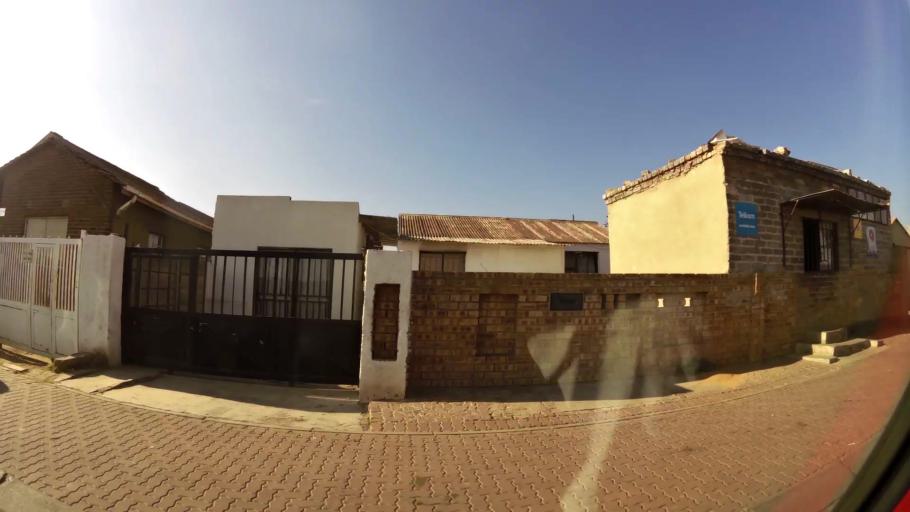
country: ZA
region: Gauteng
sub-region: City of Johannesburg Metropolitan Municipality
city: Soweto
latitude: -26.2301
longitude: 27.9300
